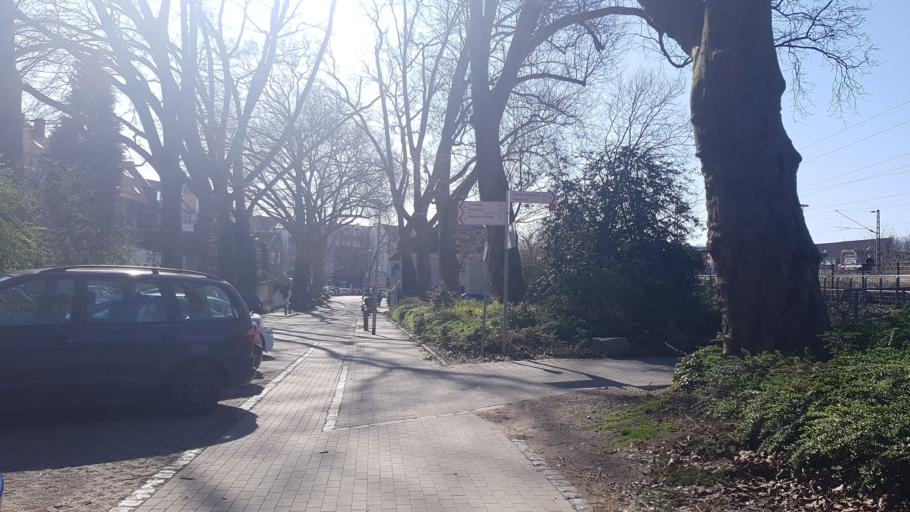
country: DE
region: North Rhine-Westphalia
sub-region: Regierungsbezirk Munster
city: Bottrop
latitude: 51.4738
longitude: 6.9483
